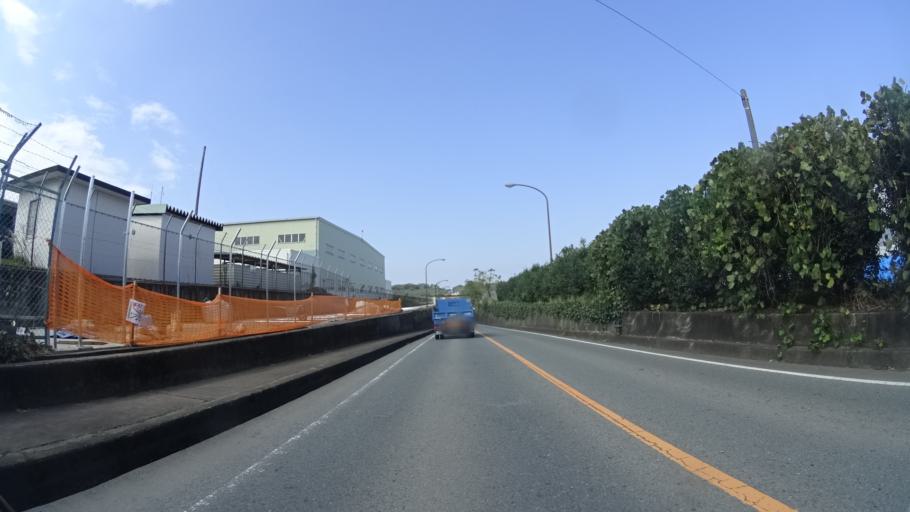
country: JP
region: Kumamoto
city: Ozu
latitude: 32.8335
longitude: 130.8560
